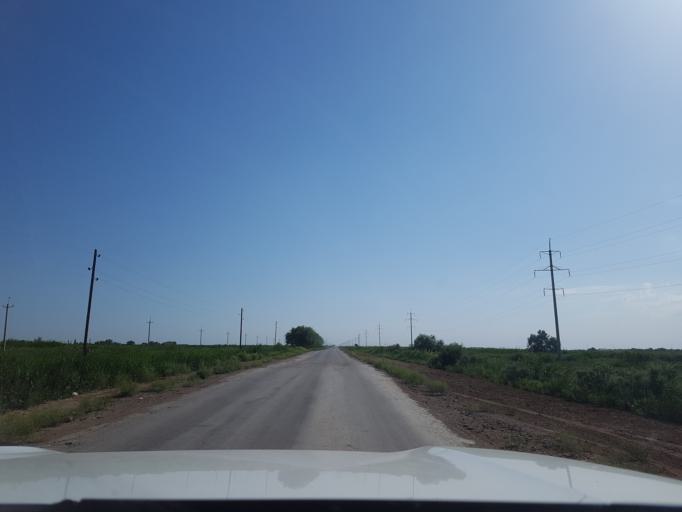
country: TM
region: Dasoguz
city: Koeneuergench
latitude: 42.1039
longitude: 58.9074
